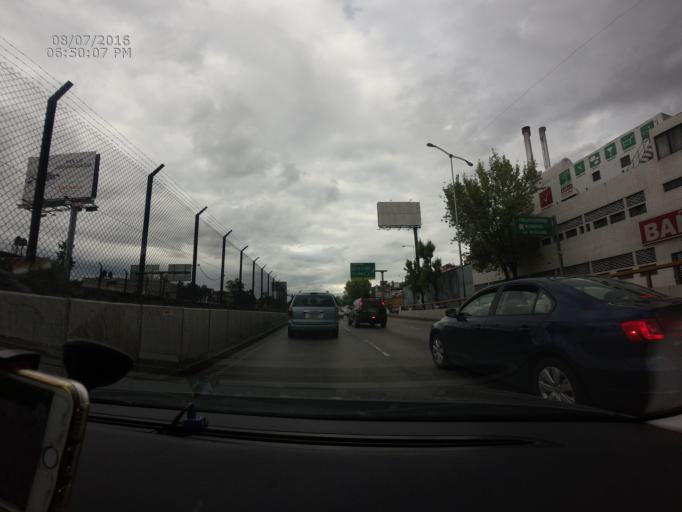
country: MX
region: Mexico City
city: Cuauhtemoc
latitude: 19.4607
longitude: -99.1253
